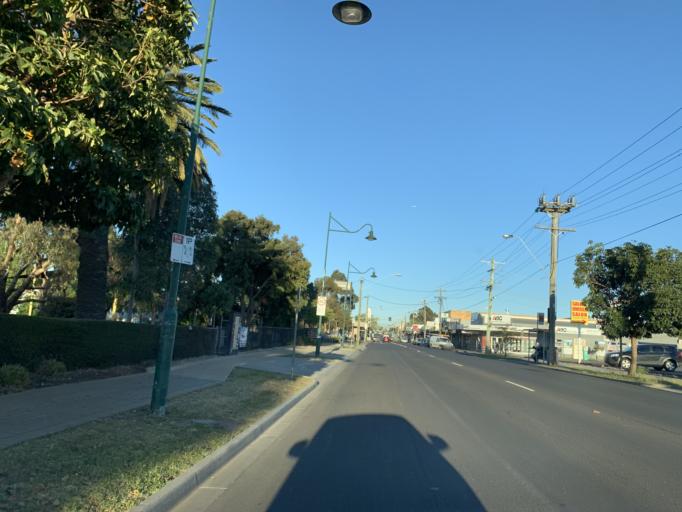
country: AU
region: Victoria
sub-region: Brimbank
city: St Albans
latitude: -37.7447
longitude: 144.8035
